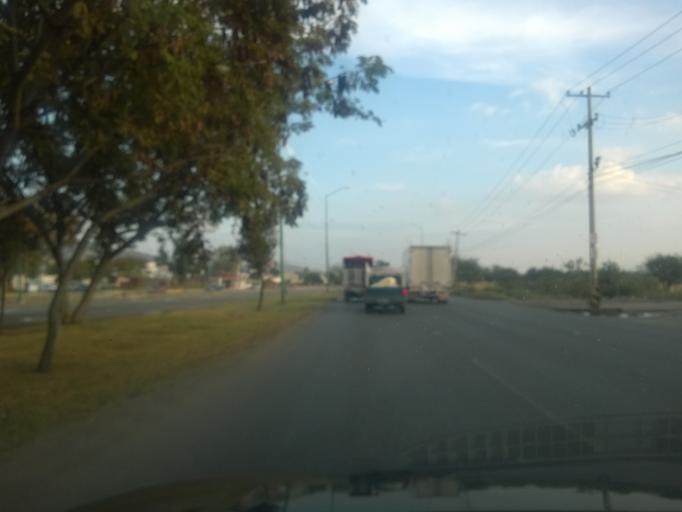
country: MX
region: Guanajuato
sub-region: Leon
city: Medina
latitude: 21.1572
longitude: -101.6424
